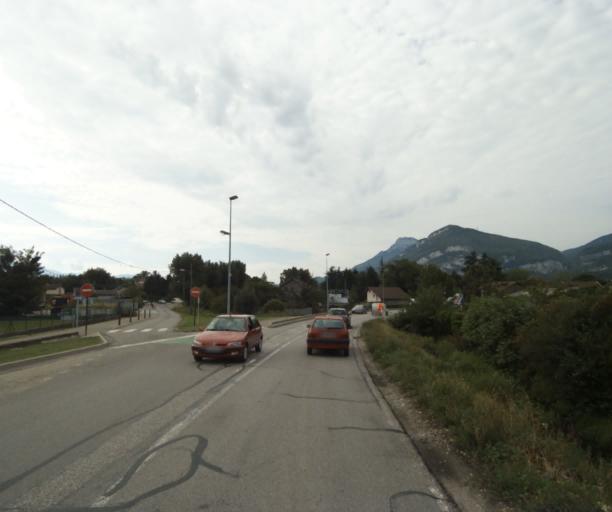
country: FR
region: Rhone-Alpes
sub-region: Departement de l'Isere
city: Fontanil-Cornillon
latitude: 45.2358
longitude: 5.6697
